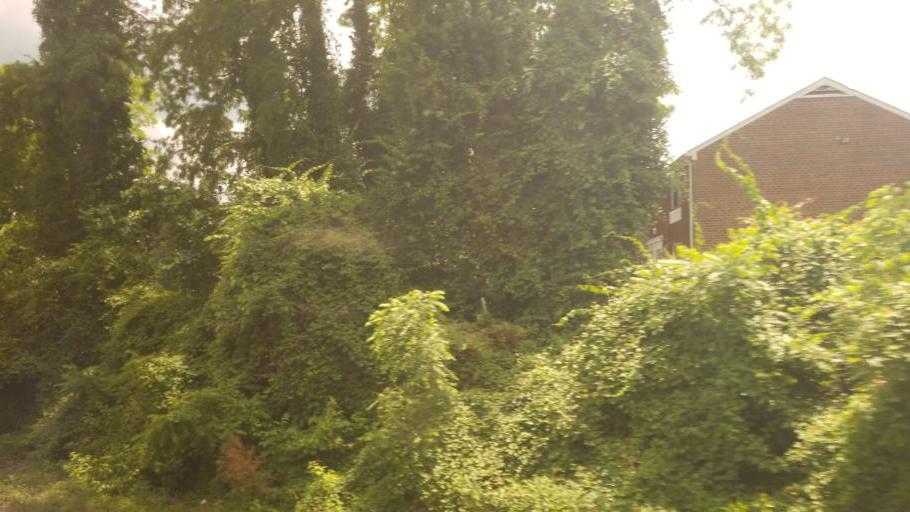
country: US
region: Maryland
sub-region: Montgomery County
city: Forest Glen
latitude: 39.0011
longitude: -77.0430
